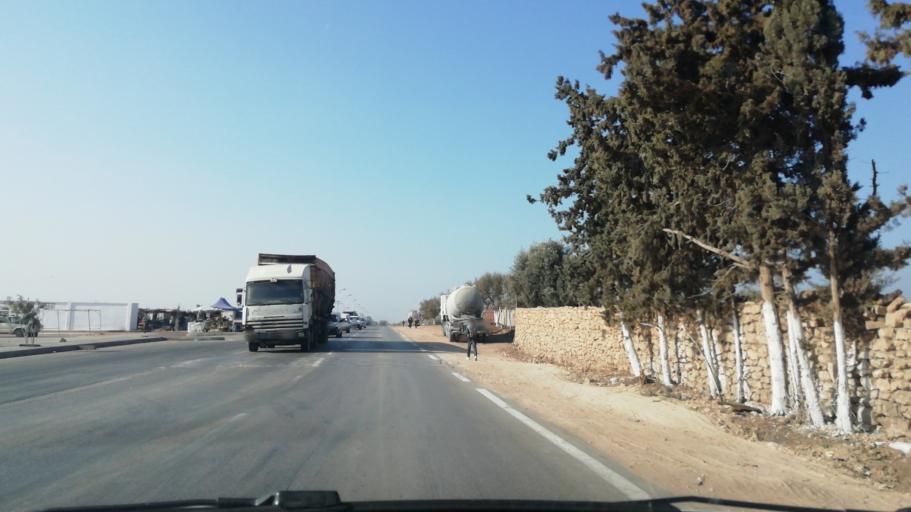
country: DZ
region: Mostaganem
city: Mostaganem
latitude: 35.7370
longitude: -0.0315
